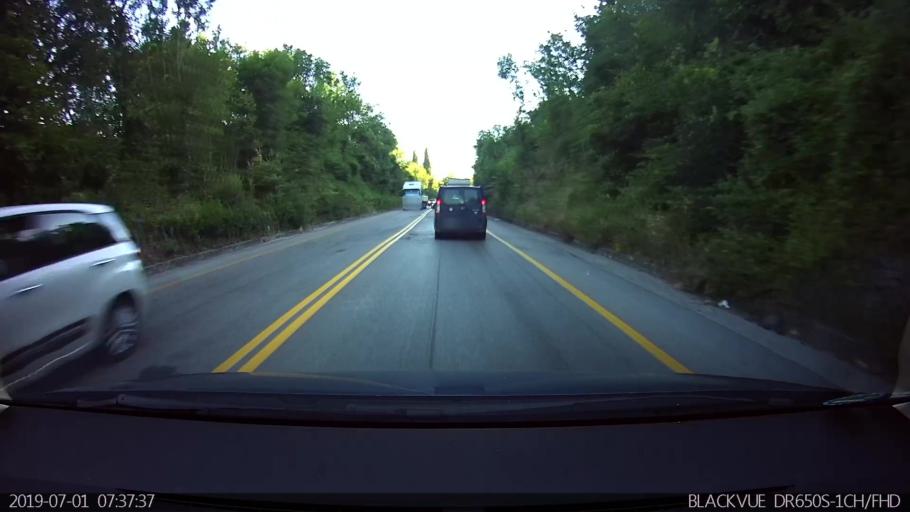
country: IT
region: Latium
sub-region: Provincia di Frosinone
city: Giuliano di Roma
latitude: 41.5390
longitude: 13.2671
